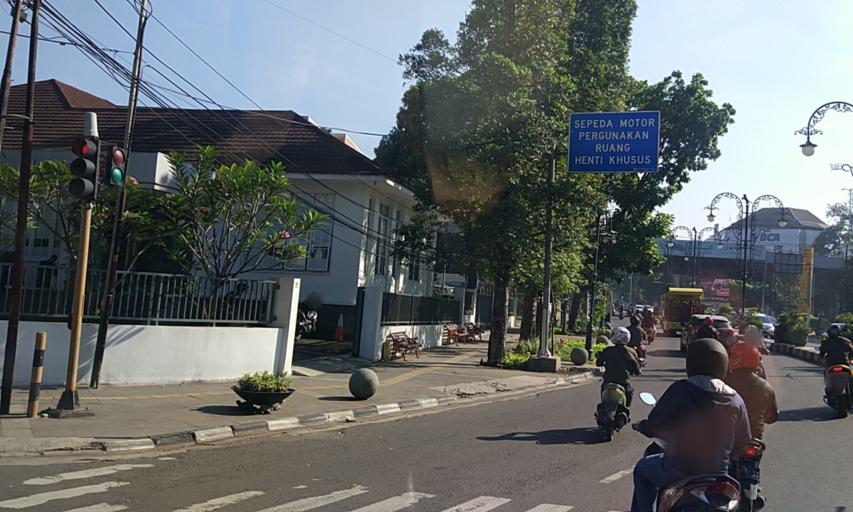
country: ID
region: West Java
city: Bandung
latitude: -6.9002
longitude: 107.6127
